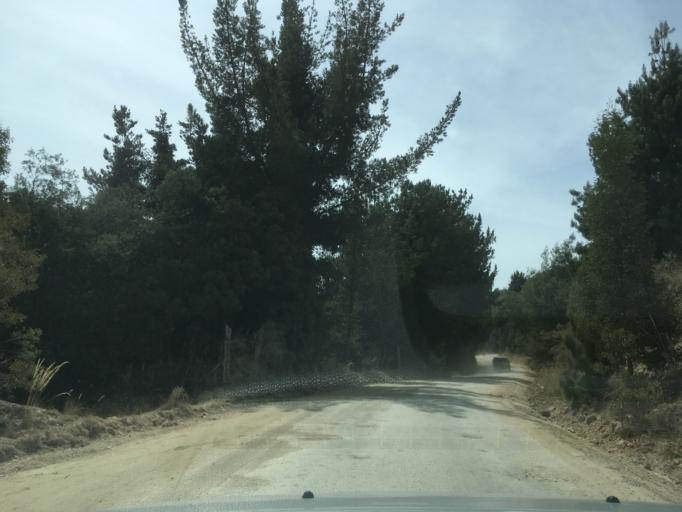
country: CO
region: Boyaca
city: Aquitania
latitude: 5.5925
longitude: -72.9189
